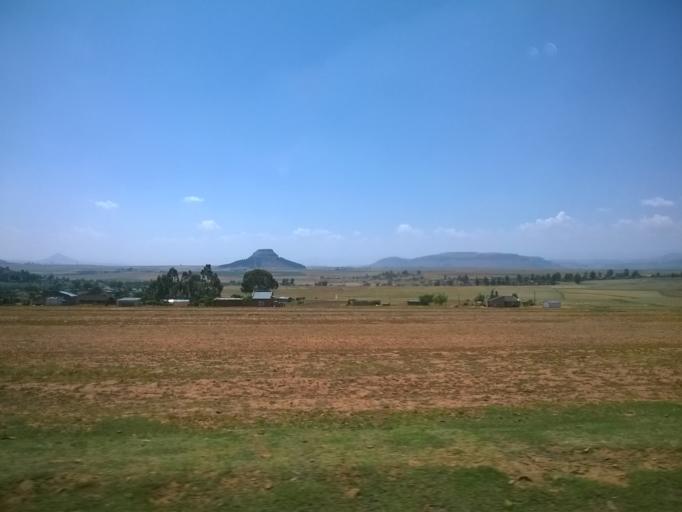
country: LS
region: Leribe
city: Maputsoe
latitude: -28.9629
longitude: 27.9618
